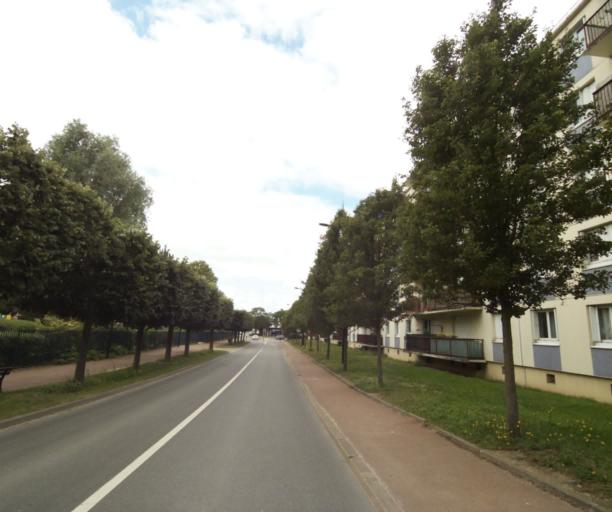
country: FR
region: Ile-de-France
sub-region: Departement des Yvelines
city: Saint-Cyr-l'Ecole
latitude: 48.8060
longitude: 2.0618
